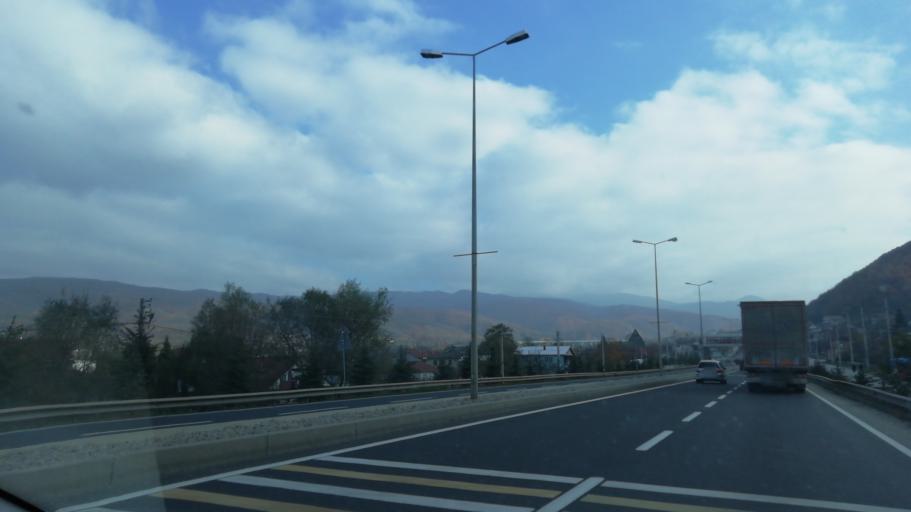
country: TR
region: Duzce
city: Kaynasli
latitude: 40.7728
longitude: 31.3258
